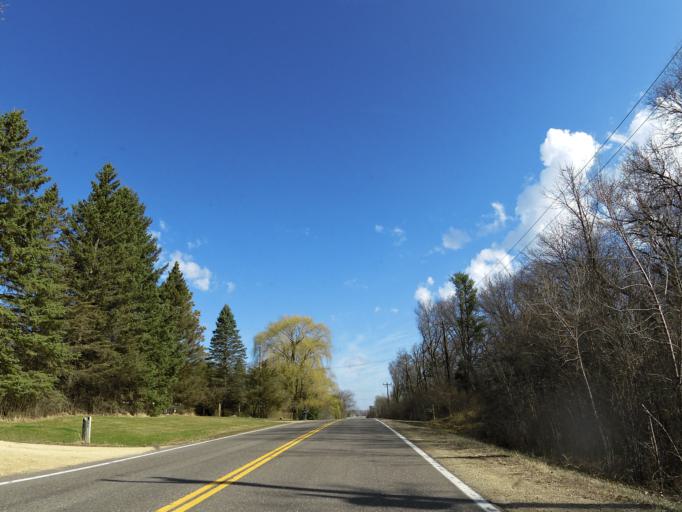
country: US
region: Minnesota
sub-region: Washington County
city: Lake Elmo
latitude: 44.9424
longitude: -92.8428
